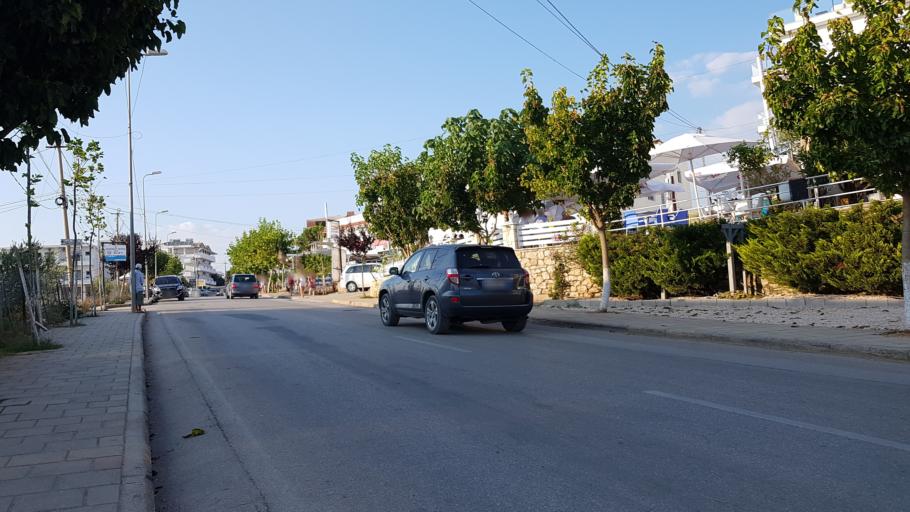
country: AL
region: Vlore
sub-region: Rrethi i Sarandes
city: Xarre
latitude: 39.7713
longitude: 20.0040
